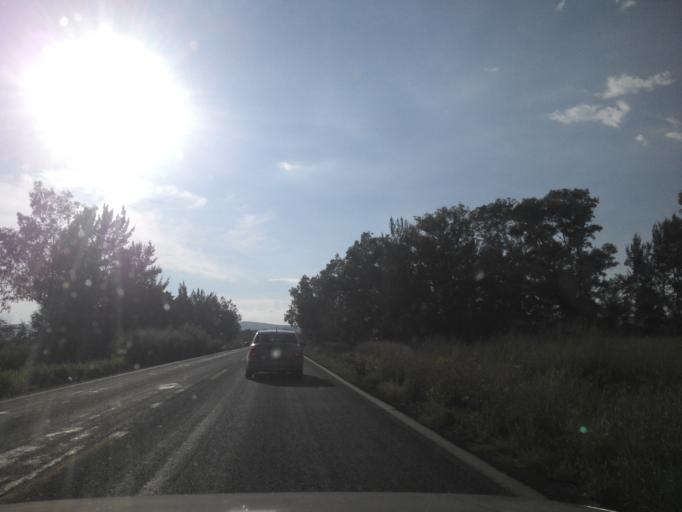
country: MX
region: Jalisco
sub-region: Tototlan
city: Nuevo Refugio de Afuera (Nuevo Refugio)
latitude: 20.5588
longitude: -102.7259
